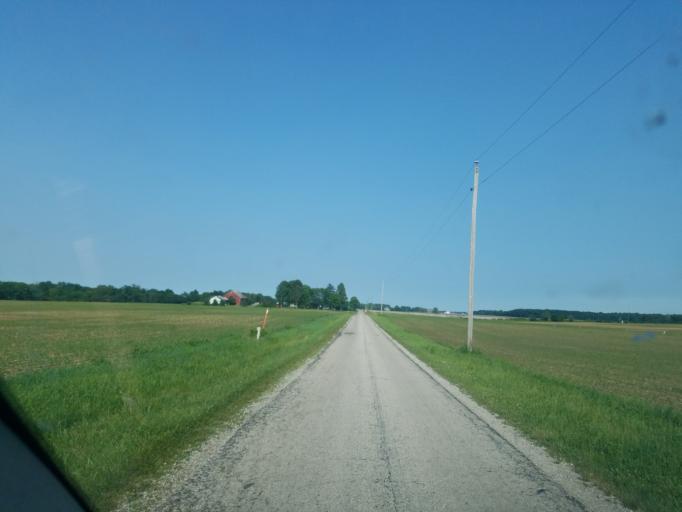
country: US
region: Ohio
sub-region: Crawford County
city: Bucyrus
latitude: 40.8923
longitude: -82.9523
